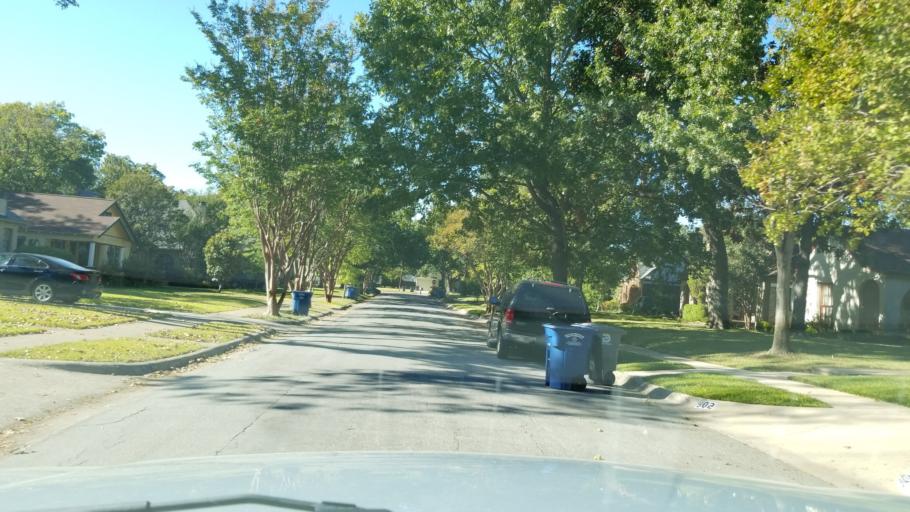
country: US
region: Texas
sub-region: Dallas County
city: Highland Park
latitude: 32.8053
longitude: -96.7452
